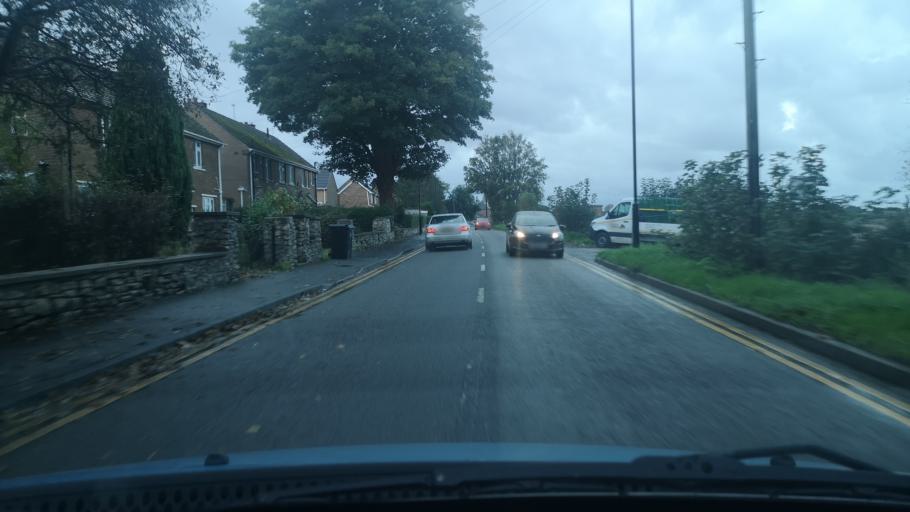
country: GB
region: England
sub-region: Doncaster
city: Campsall
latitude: 53.6226
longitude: -1.1729
